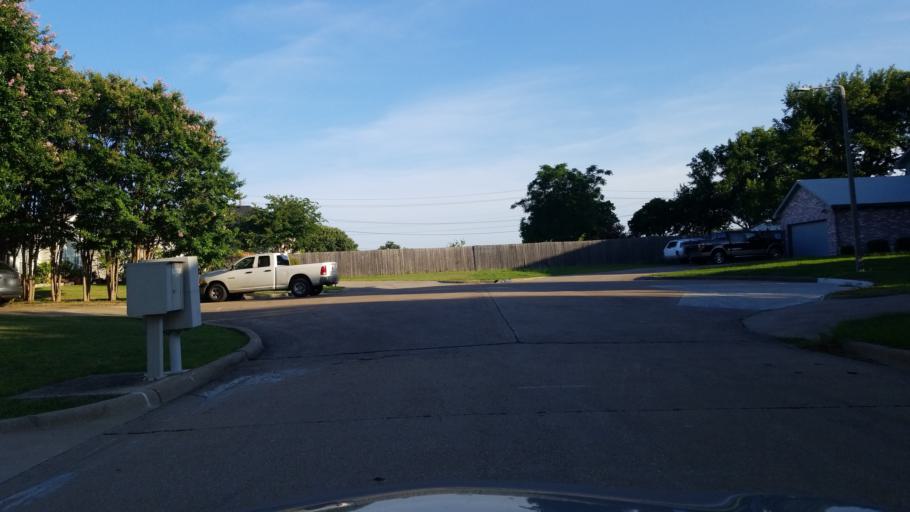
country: US
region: Texas
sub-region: Dallas County
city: Grand Prairie
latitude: 32.6923
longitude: -97.0320
